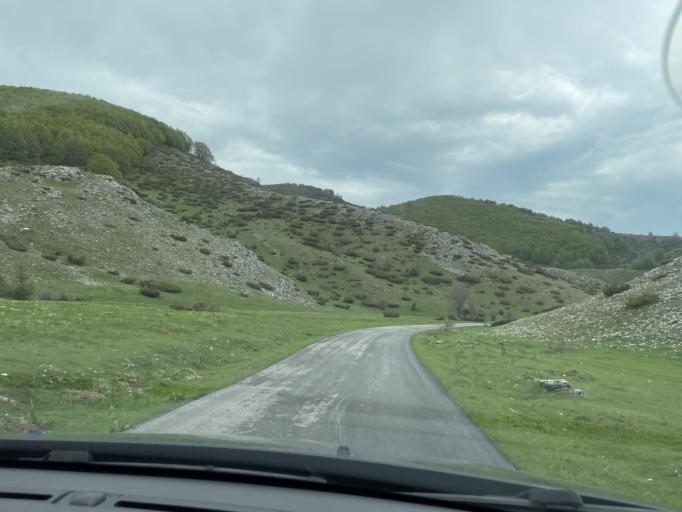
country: MK
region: Opstina Rostusa
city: Rostusha
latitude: 41.6040
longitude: 20.6848
